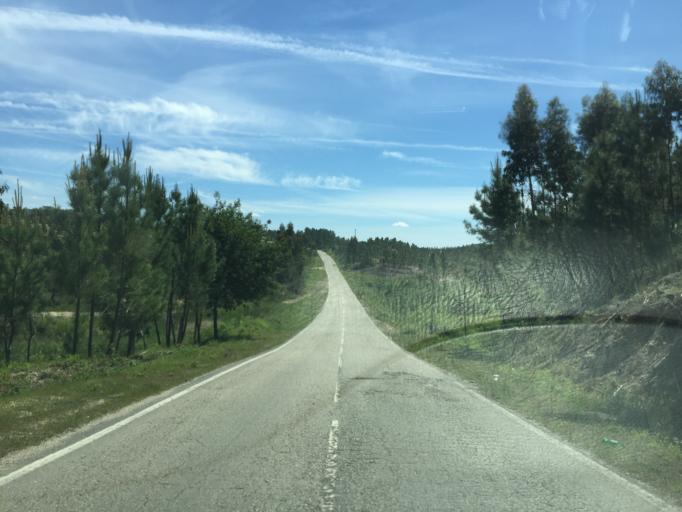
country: PT
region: Leiria
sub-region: Pombal
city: Lourical
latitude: 40.0638
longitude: -8.6988
